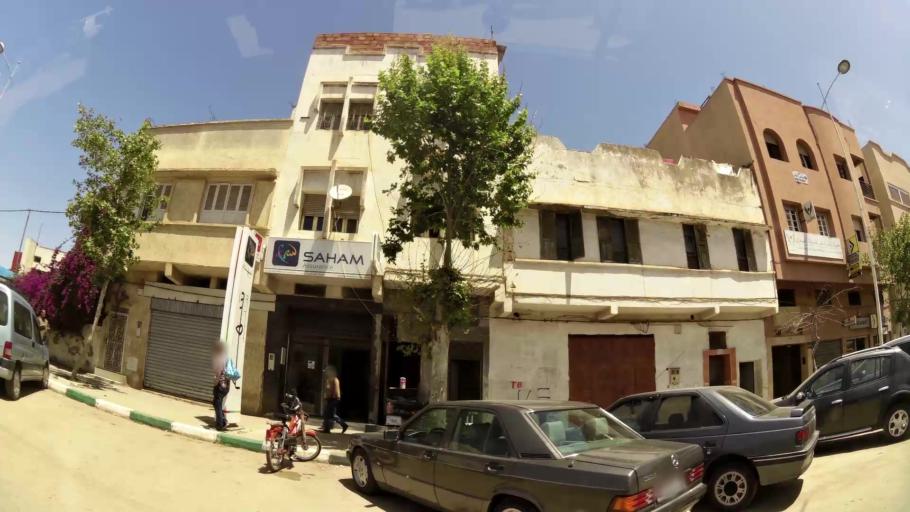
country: MA
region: Rabat-Sale-Zemmour-Zaer
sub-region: Khemisset
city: Khemisset
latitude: 33.8261
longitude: -6.0731
